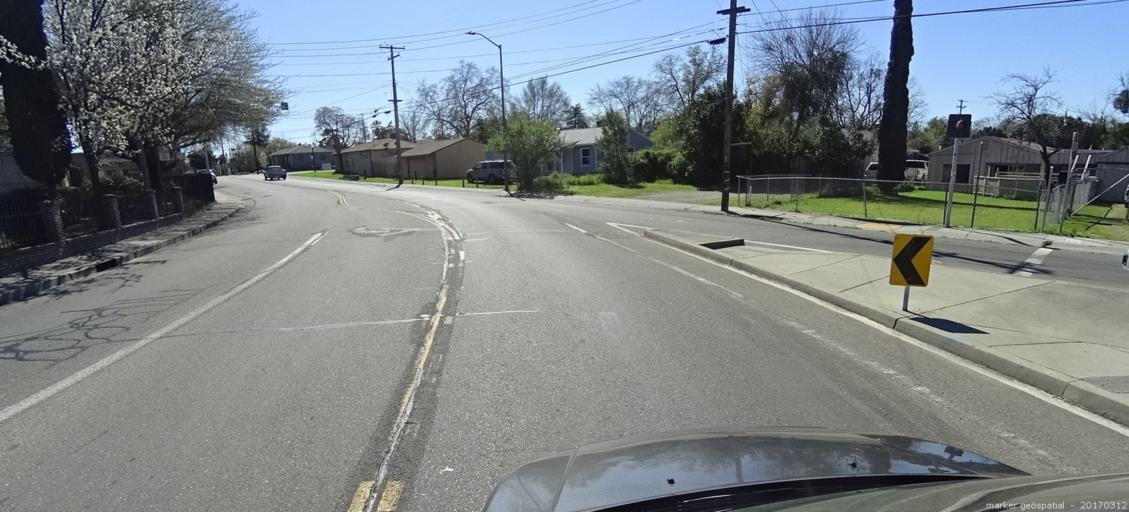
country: US
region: California
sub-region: Sacramento County
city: Sacramento
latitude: 38.6131
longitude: -121.4592
